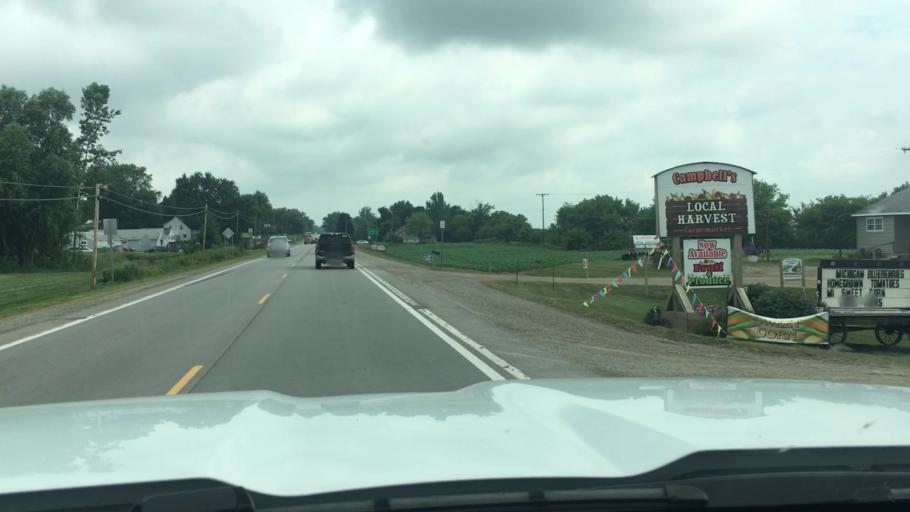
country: US
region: Michigan
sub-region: Lapeer County
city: Imlay City
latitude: 43.0339
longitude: -83.0717
